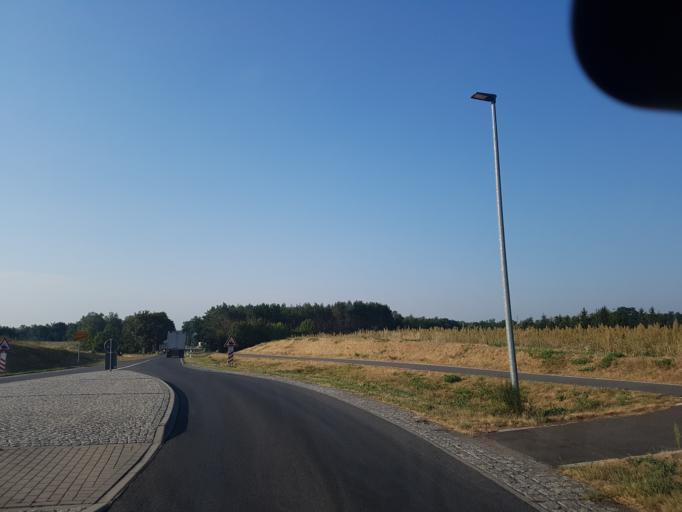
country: DE
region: Brandenburg
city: Hohenleipisch
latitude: 51.4844
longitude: 13.5466
